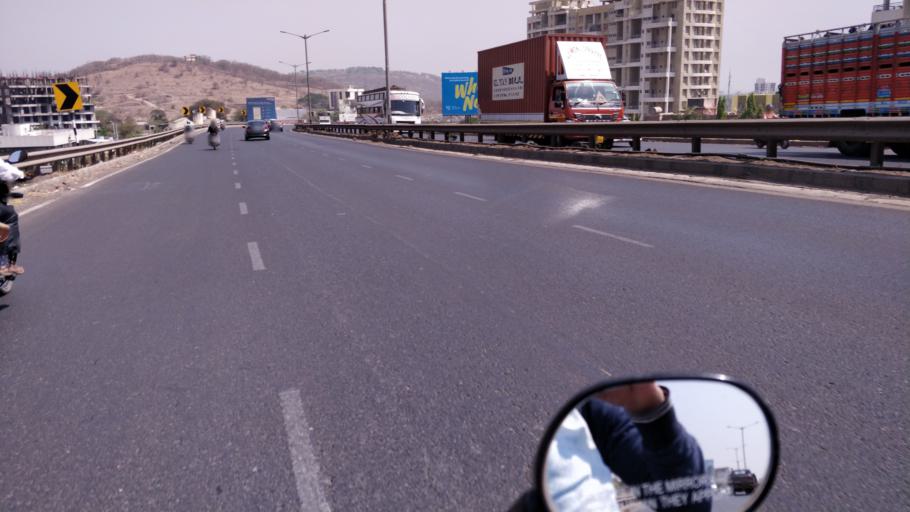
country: IN
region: Maharashtra
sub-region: Pune Division
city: Kharakvasla
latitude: 18.5207
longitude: 73.7692
